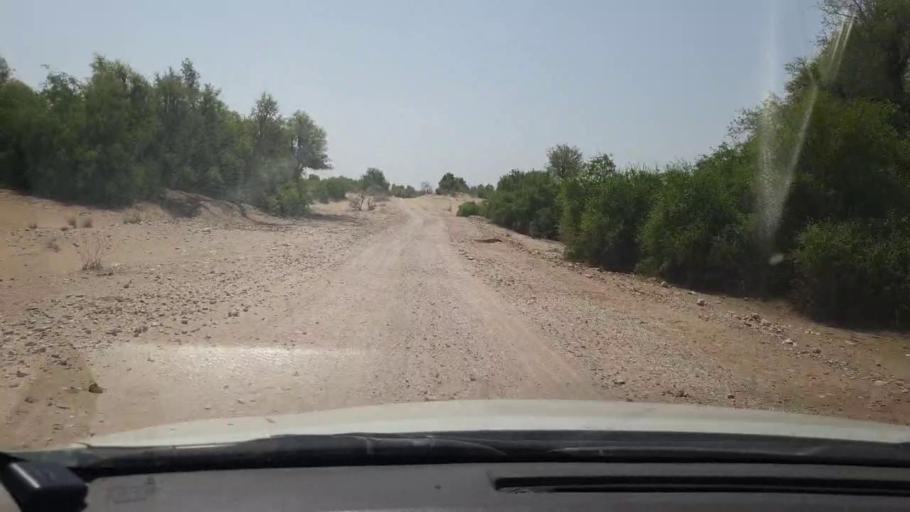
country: PK
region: Sindh
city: Rohri
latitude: 27.3169
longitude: 69.2799
